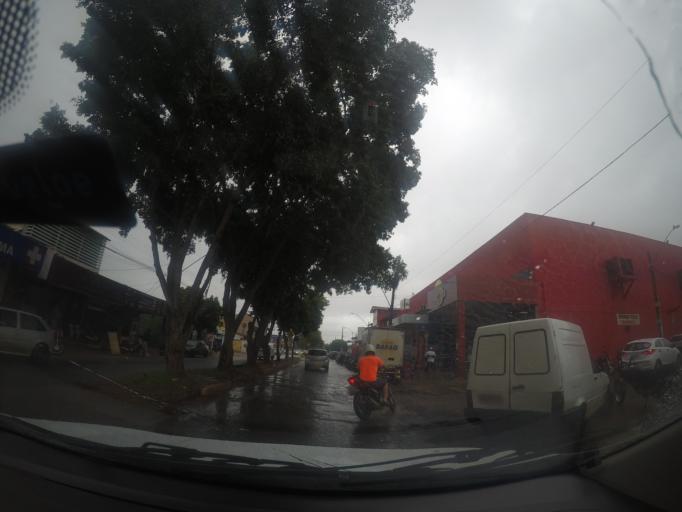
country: BR
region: Goias
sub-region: Goiania
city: Goiania
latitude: -16.6099
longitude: -49.3461
